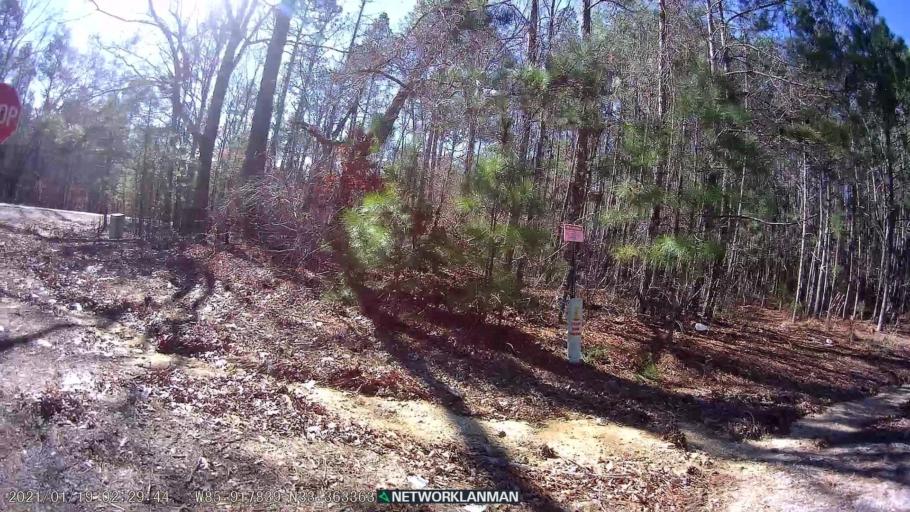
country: US
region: Alabama
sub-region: Clay County
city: Ashland
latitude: 33.3635
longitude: -85.9179
